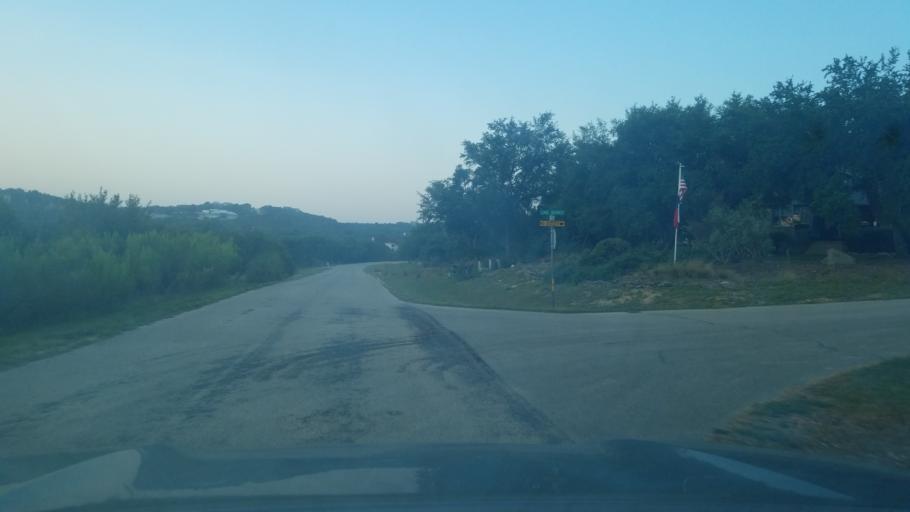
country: US
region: Texas
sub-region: Comal County
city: Bulverde
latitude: 29.8214
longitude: -98.4026
